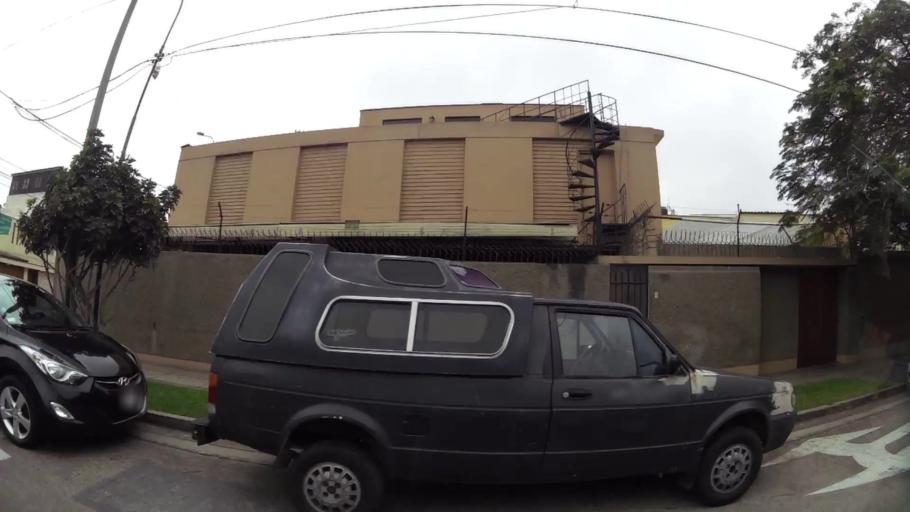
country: PE
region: Lima
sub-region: Lima
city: Surco
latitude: -12.1261
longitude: -76.9944
